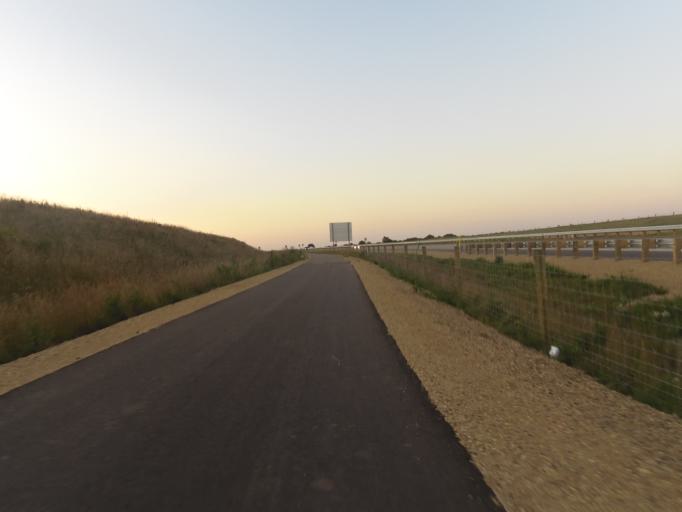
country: US
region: Minnesota
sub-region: Washington County
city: Oak Park Heights
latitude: 45.0494
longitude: -92.7794
